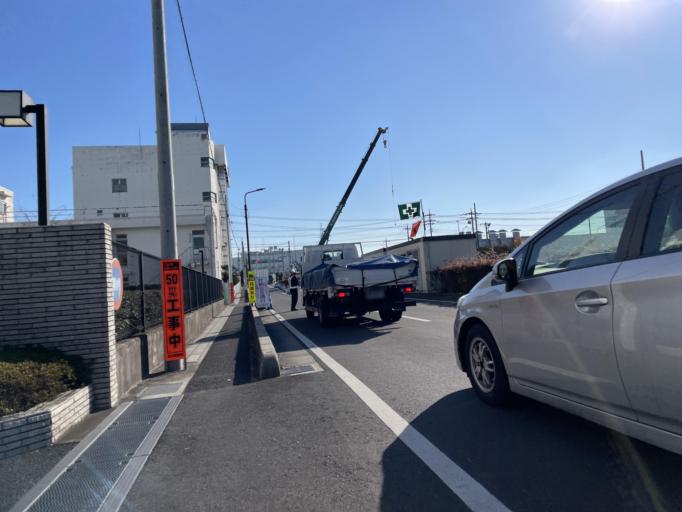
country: JP
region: Saitama
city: Yashio-shi
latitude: 35.8437
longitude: 139.8210
